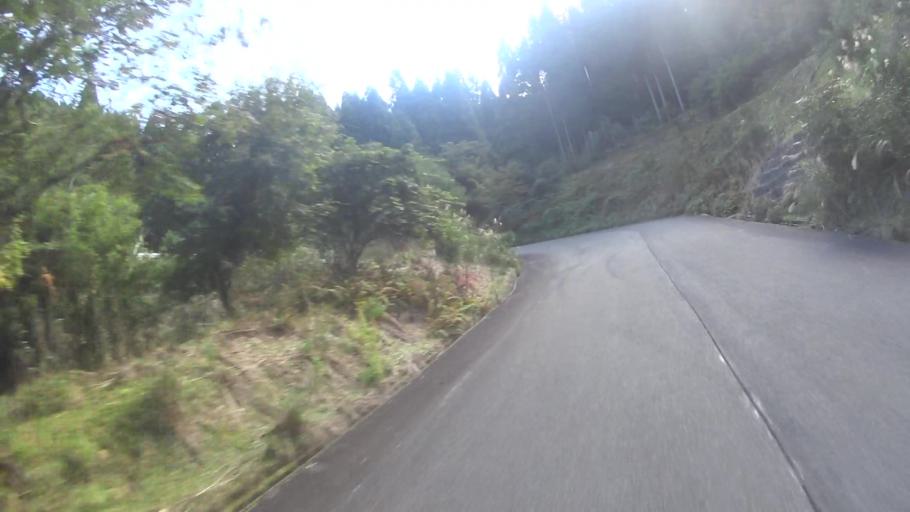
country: JP
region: Hyogo
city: Toyooka
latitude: 35.5361
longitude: 134.9135
